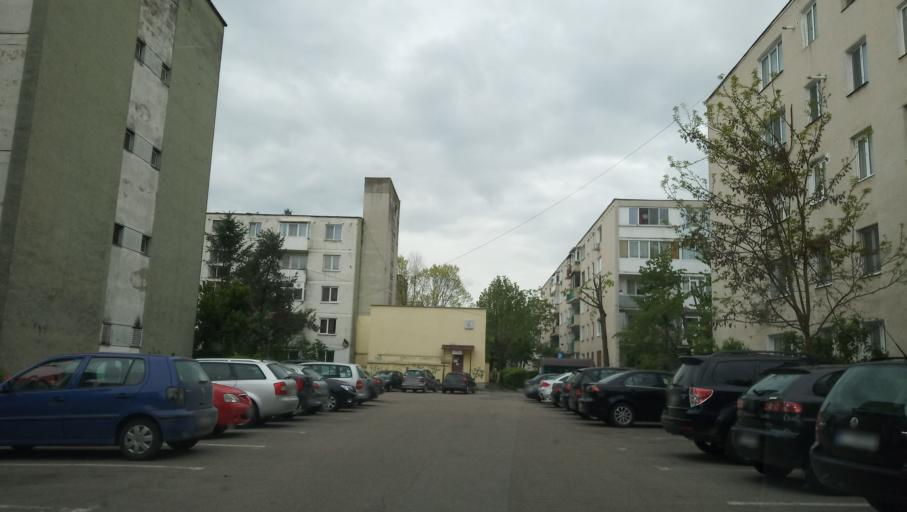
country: RO
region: Valcea
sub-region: Municipiul Ramnicu Valcea
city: Ramnicu Valcea
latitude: 45.0992
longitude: 24.3653
